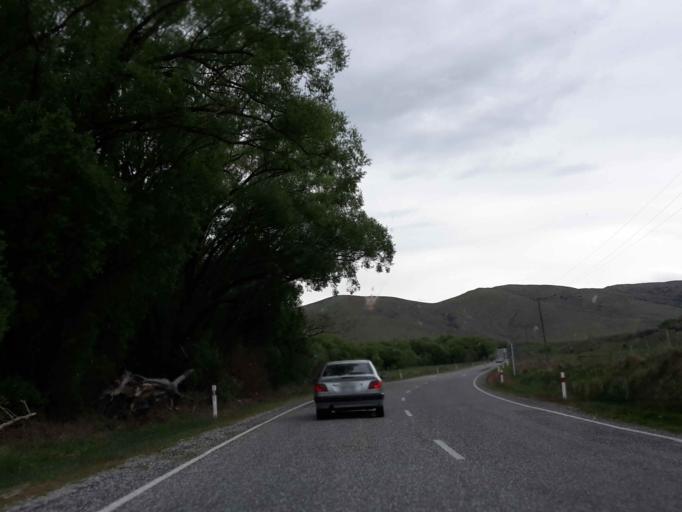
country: NZ
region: Otago
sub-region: Queenstown-Lakes District
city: Wanaka
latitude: -44.7158
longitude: 169.5036
